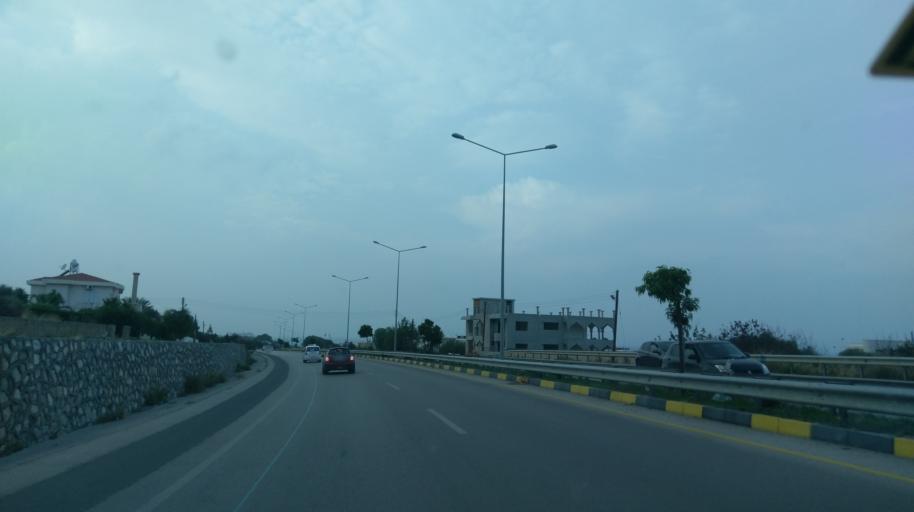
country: CY
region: Keryneia
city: Kyrenia
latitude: 35.3389
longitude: 33.2545
